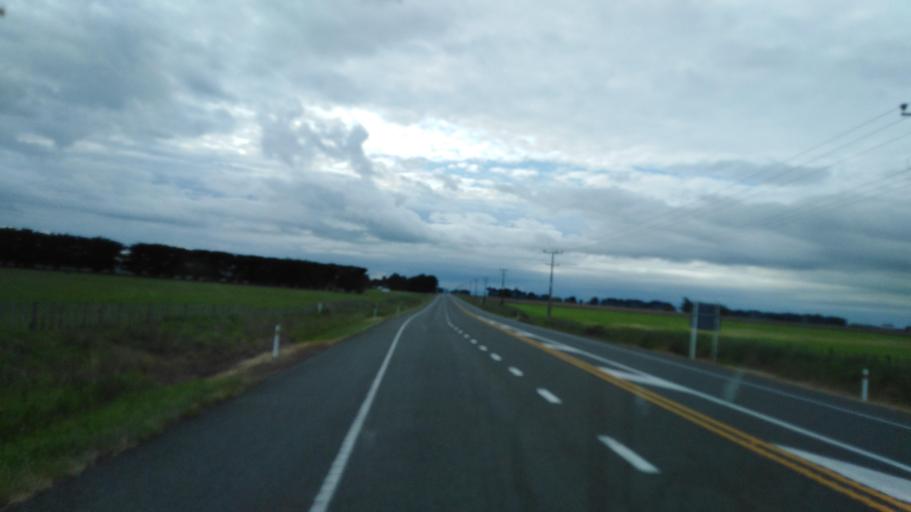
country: NZ
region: Manawatu-Wanganui
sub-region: Rangitikei District
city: Bulls
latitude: -40.1260
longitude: 175.3548
